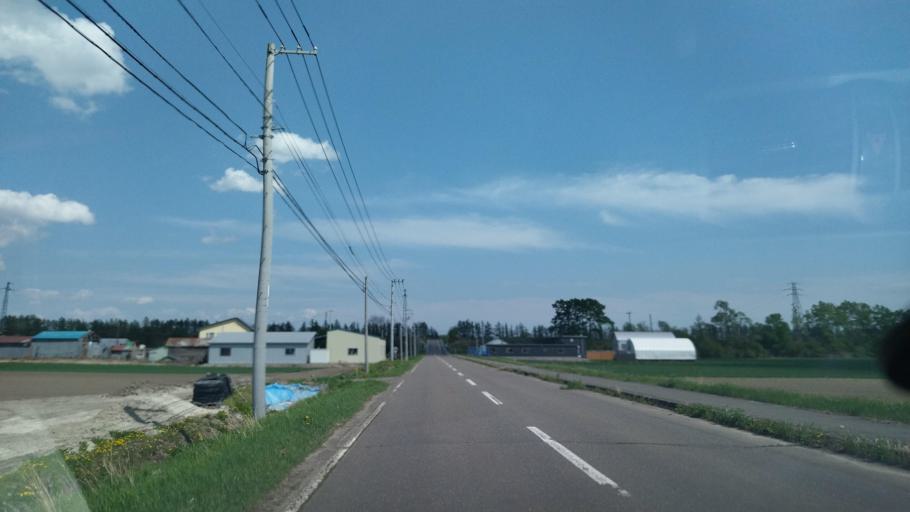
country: JP
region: Hokkaido
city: Otofuke
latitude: 43.1015
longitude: 143.2167
